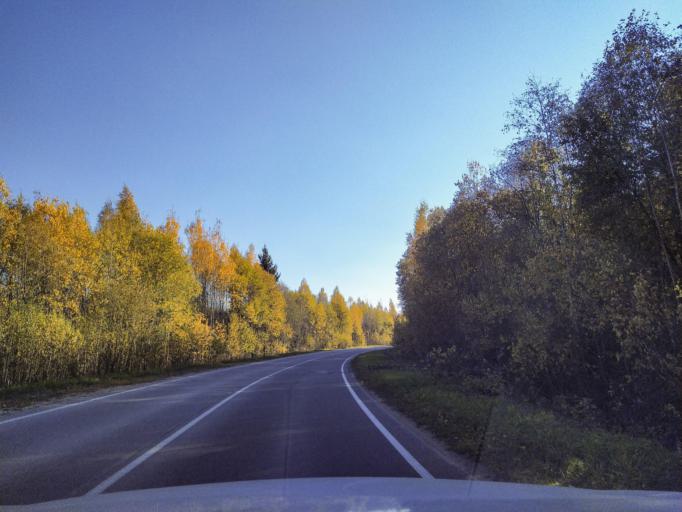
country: RU
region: Leningrad
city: Siverskiy
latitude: 59.3032
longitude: 30.0349
